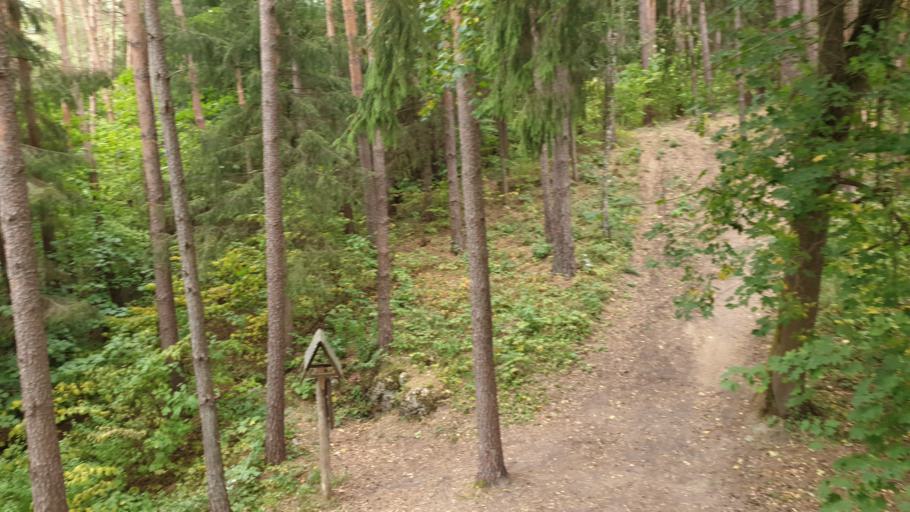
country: LT
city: Grigiskes
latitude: 54.7398
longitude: 25.0231
